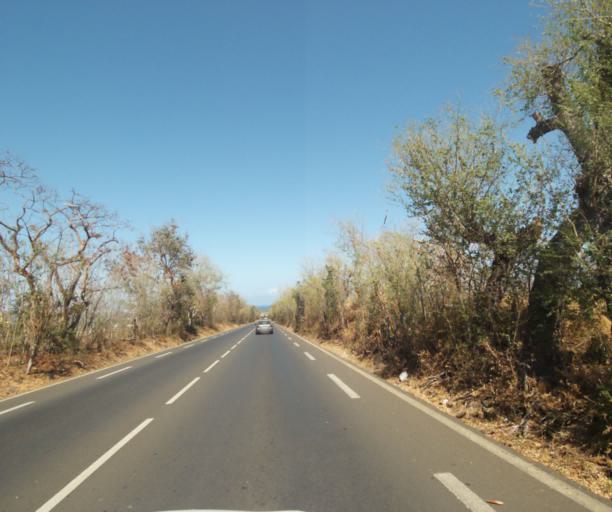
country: RE
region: Reunion
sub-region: Reunion
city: Le Port
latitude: -20.9817
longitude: 55.3099
